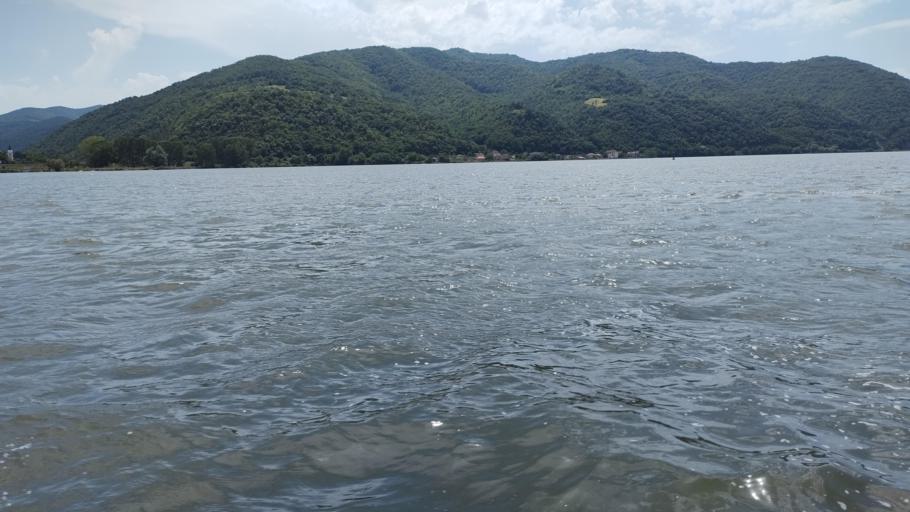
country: RO
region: Caras-Severin
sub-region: Comuna Berzasca
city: Liubcova
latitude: 44.6465
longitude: 21.9105
